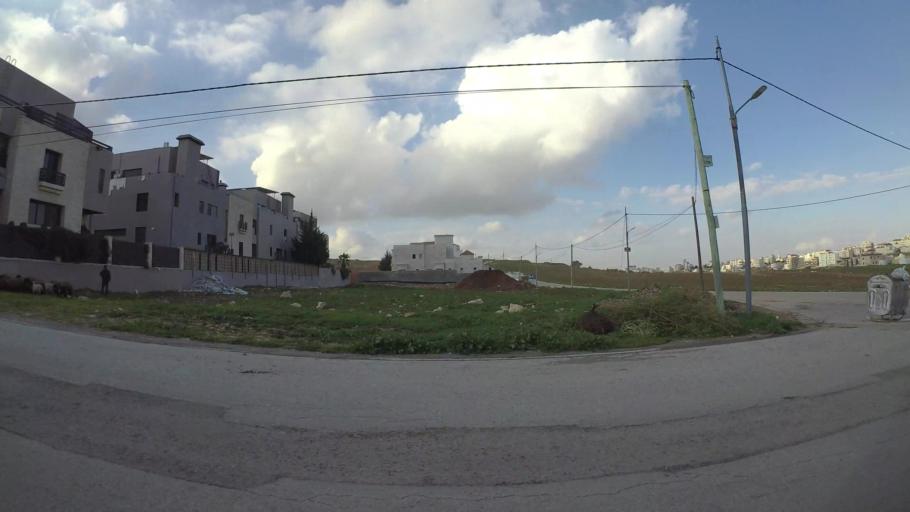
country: JO
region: Amman
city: Al Bunayyat ash Shamaliyah
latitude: 31.9115
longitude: 35.8773
